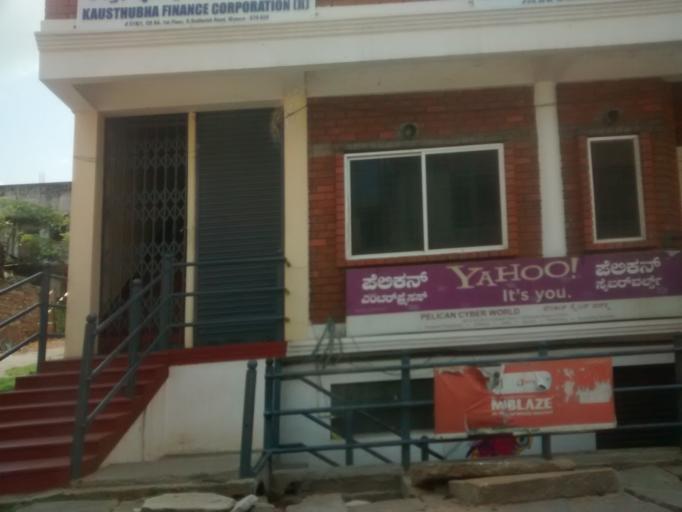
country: IN
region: Karnataka
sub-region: Mysore
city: Mysore
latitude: 12.3034
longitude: 76.6444
